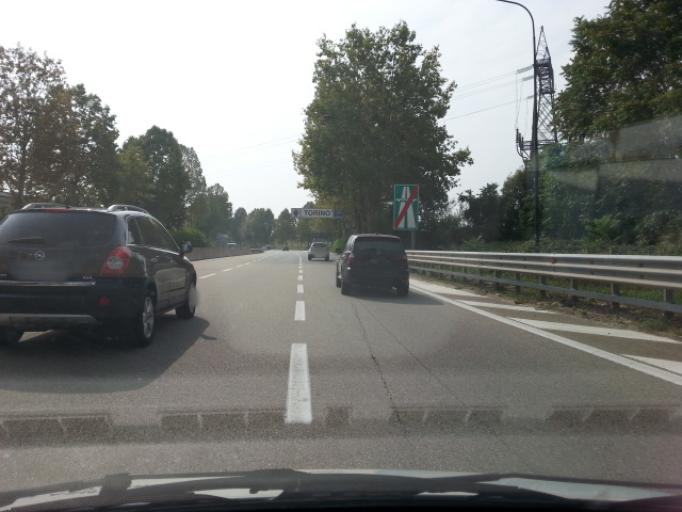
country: IT
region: Piedmont
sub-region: Provincia di Torino
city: Savonera
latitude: 45.1021
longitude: 7.6136
